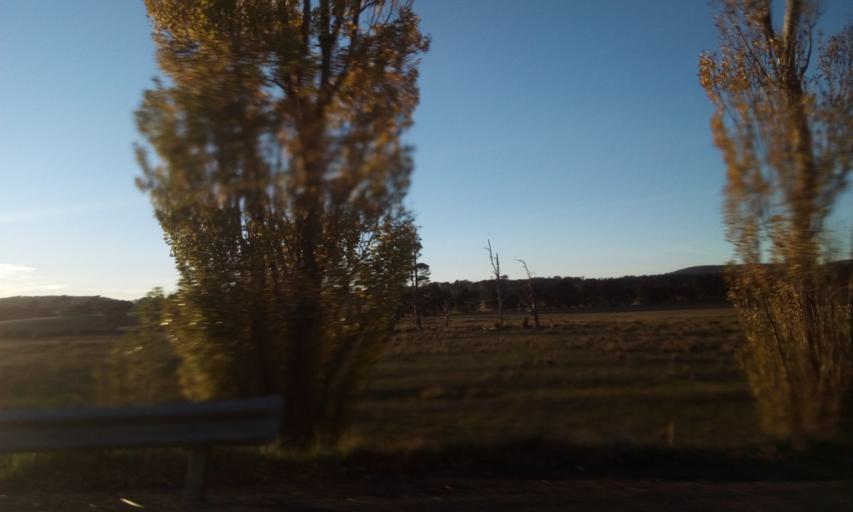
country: AU
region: New South Wales
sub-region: Goulburn Mulwaree
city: Goulburn
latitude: -34.7994
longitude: 149.6137
